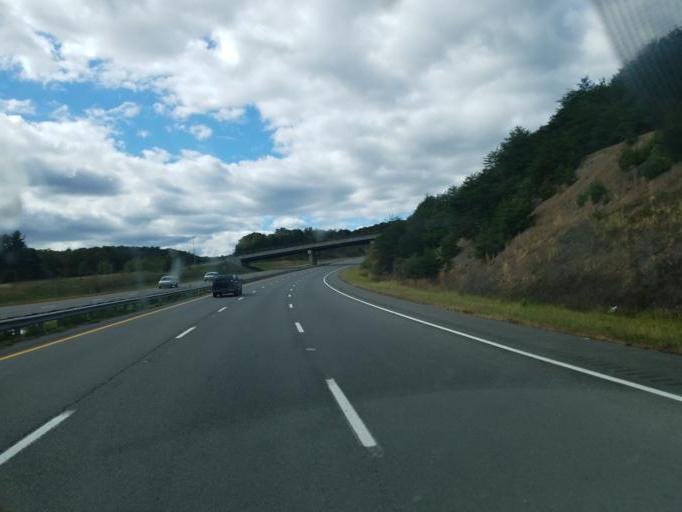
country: US
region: Maryland
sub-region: Washington County
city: Hancock
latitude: 39.6984
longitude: -78.2441
